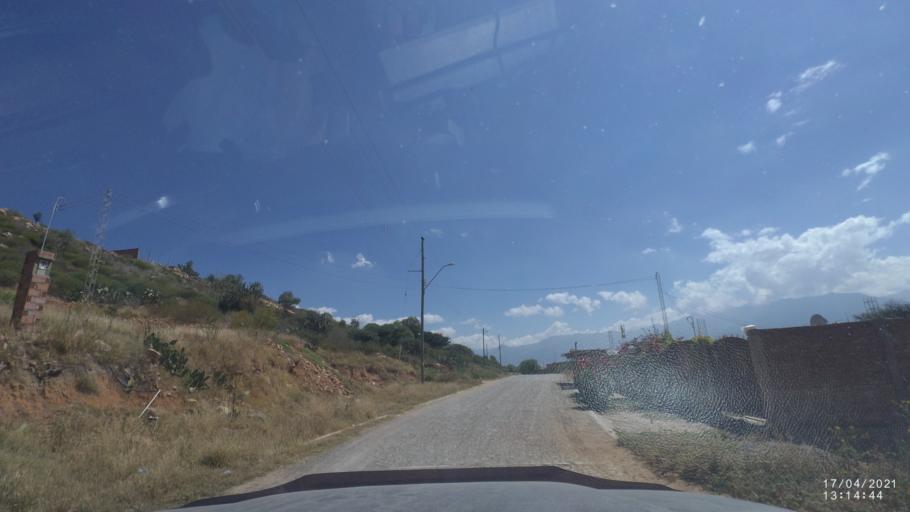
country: BO
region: Cochabamba
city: Cochabamba
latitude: -17.4169
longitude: -66.2269
